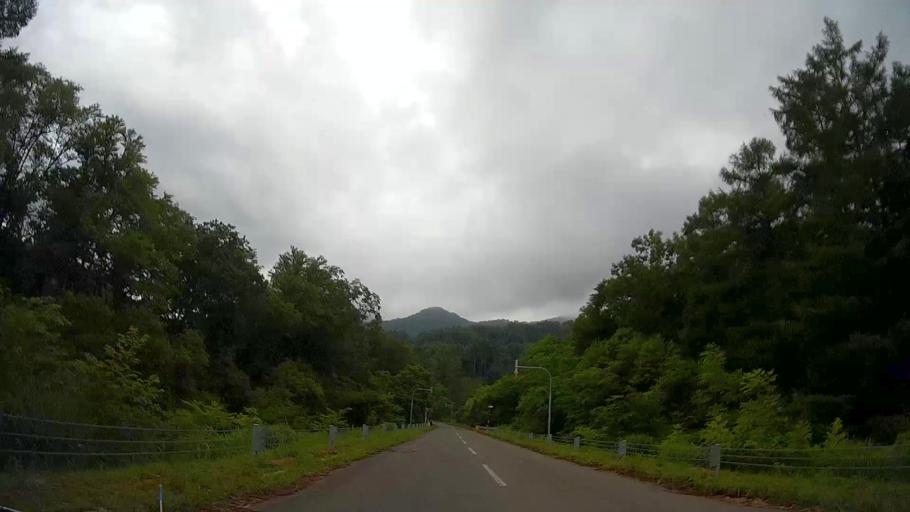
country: JP
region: Hokkaido
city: Nanae
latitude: 42.0714
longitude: 140.5108
